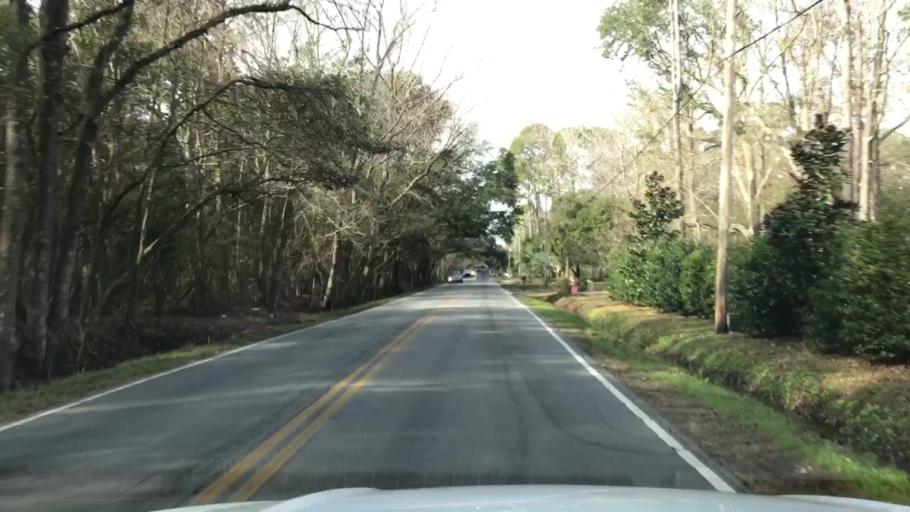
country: US
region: South Carolina
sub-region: Charleston County
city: Shell Point
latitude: 32.7645
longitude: -80.0629
